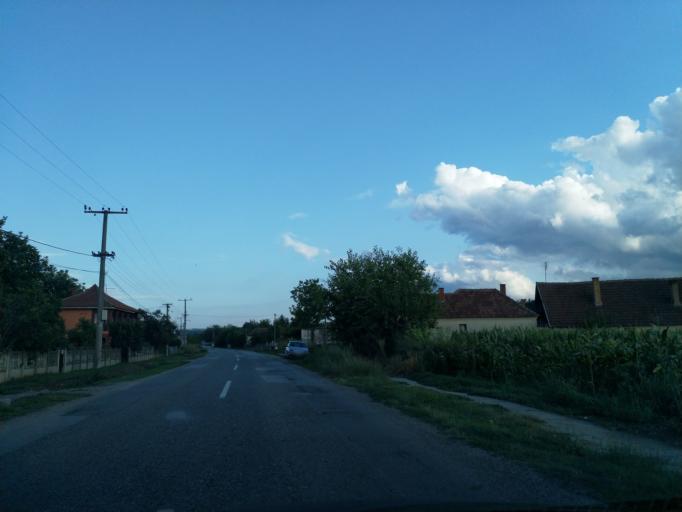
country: RS
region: Central Serbia
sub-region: Rasinski Okrug
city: Cicevac
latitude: 43.7558
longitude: 21.4354
